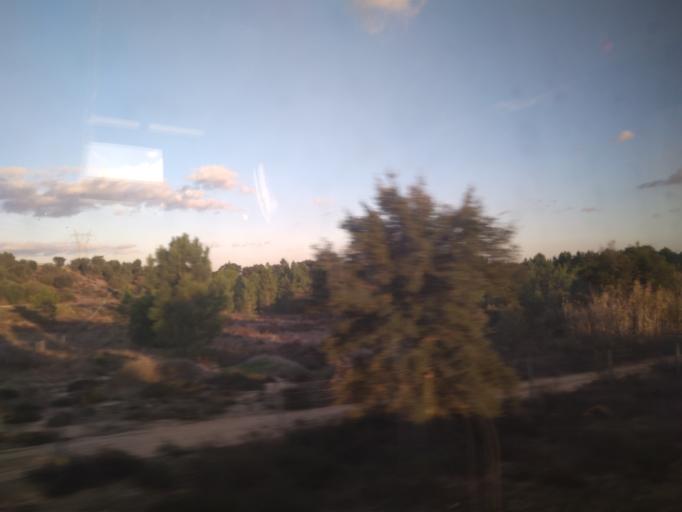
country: PT
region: Setubal
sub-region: Palmela
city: Palmela
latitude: 38.6003
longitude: -8.7331
